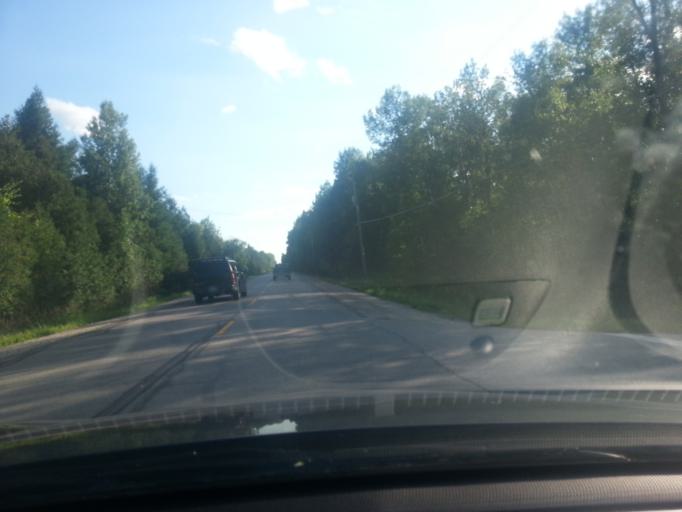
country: CA
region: Ontario
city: Carleton Place
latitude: 45.0709
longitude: -76.2730
